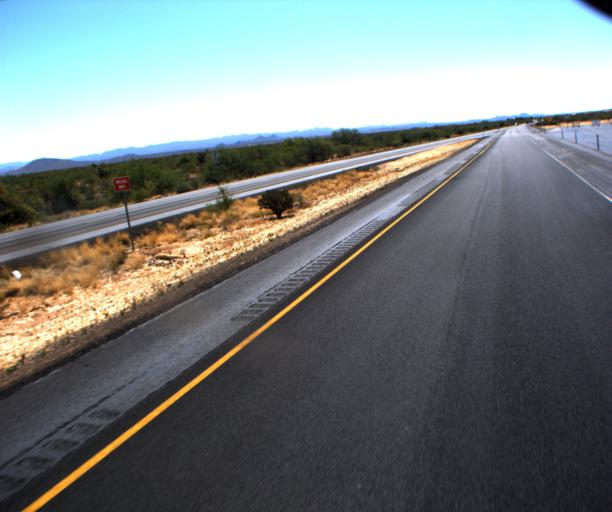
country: US
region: Arizona
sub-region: Yavapai County
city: Congress
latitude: 34.0567
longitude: -112.8552
